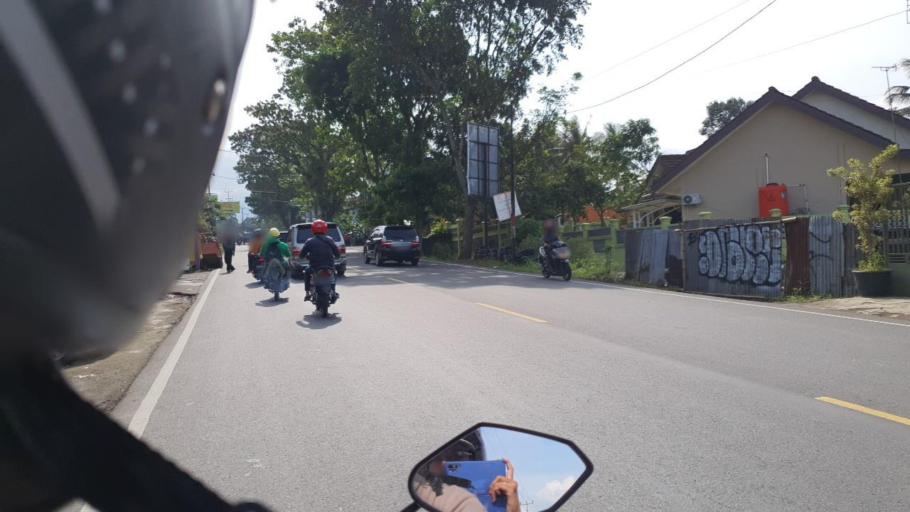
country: ID
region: West Java
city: Caringin
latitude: -6.6528
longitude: 106.8797
